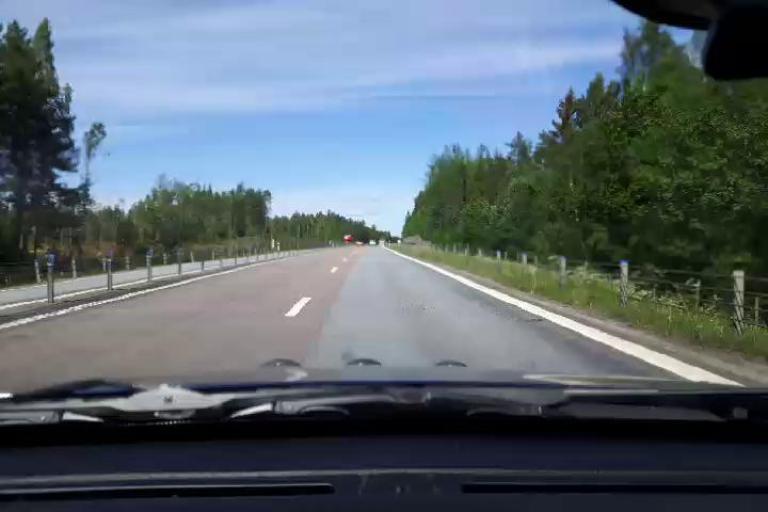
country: SE
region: Gaevleborg
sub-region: Gavle Kommun
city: Norrsundet
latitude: 60.9389
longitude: 17.0172
